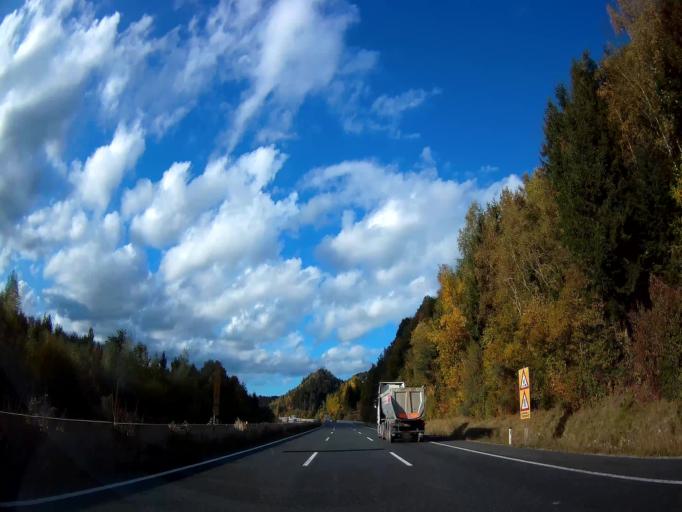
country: AT
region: Carinthia
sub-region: Politischer Bezirk Wolfsberg
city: Wolfsberg
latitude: 46.8819
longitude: 14.8302
